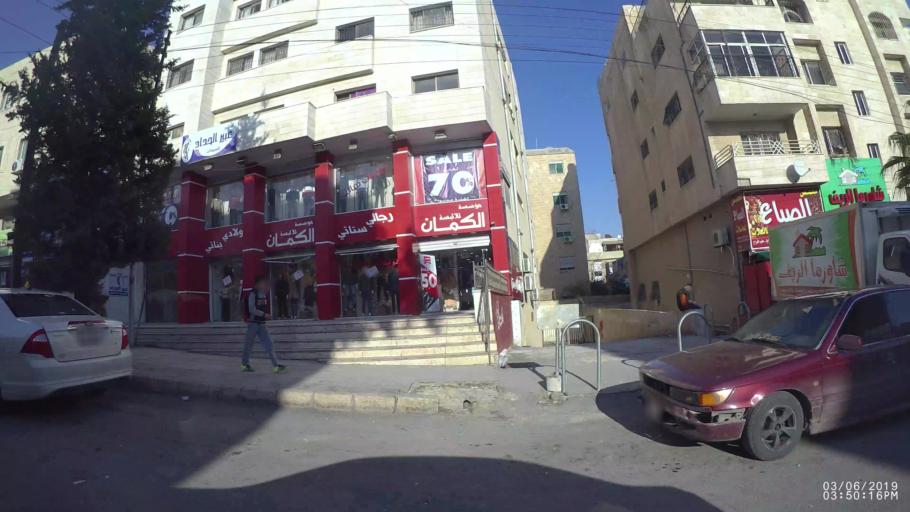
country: JO
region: Amman
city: Amman
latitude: 31.9749
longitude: 35.9498
